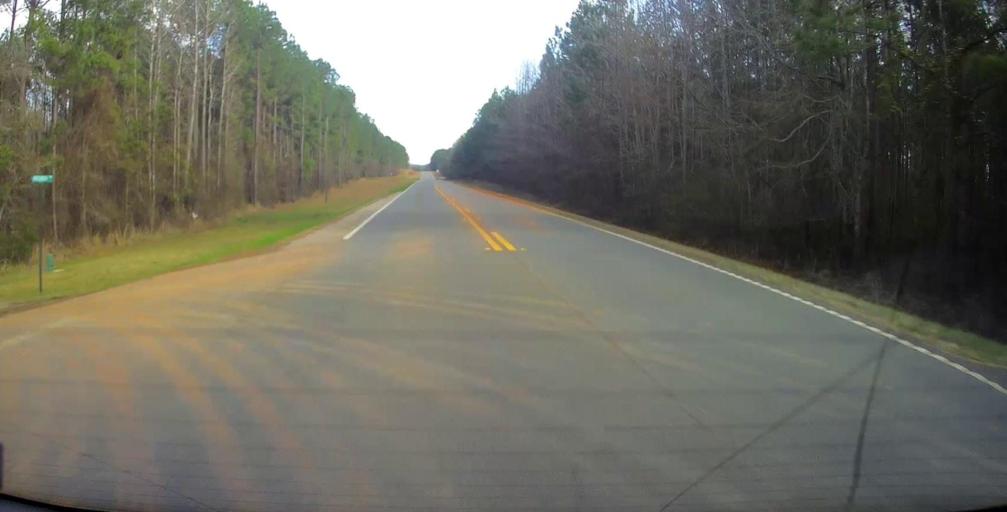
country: US
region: Georgia
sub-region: Harris County
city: Hamilton
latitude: 32.6905
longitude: -84.7886
